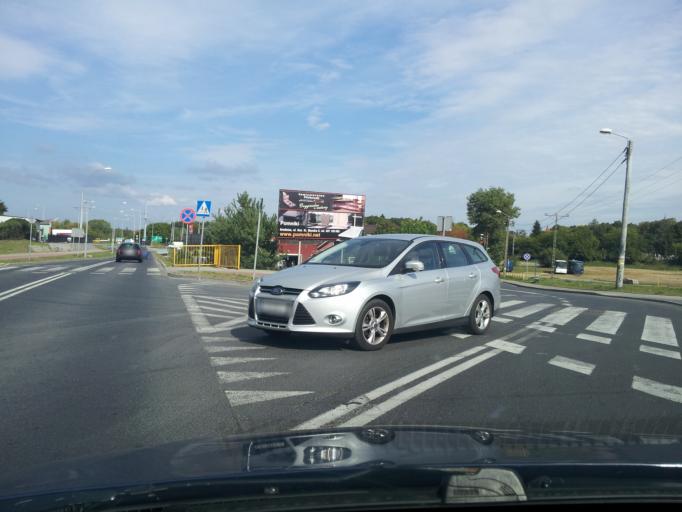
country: PL
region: Kujawsko-Pomorskie
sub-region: Powiat brodnicki
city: Brodnica
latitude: 53.2587
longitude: 19.3859
